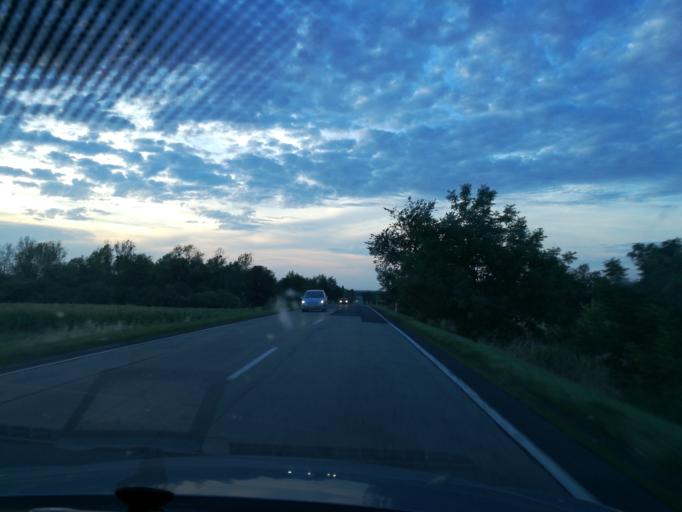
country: HU
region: Komarom-Esztergom
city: Kisber
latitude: 47.4950
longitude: 18.0494
